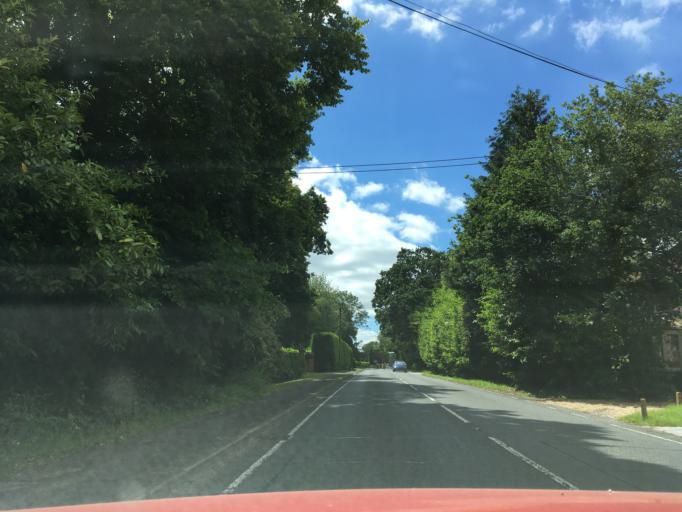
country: GB
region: England
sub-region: Hampshire
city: Highclere
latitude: 51.3412
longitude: -1.3739
